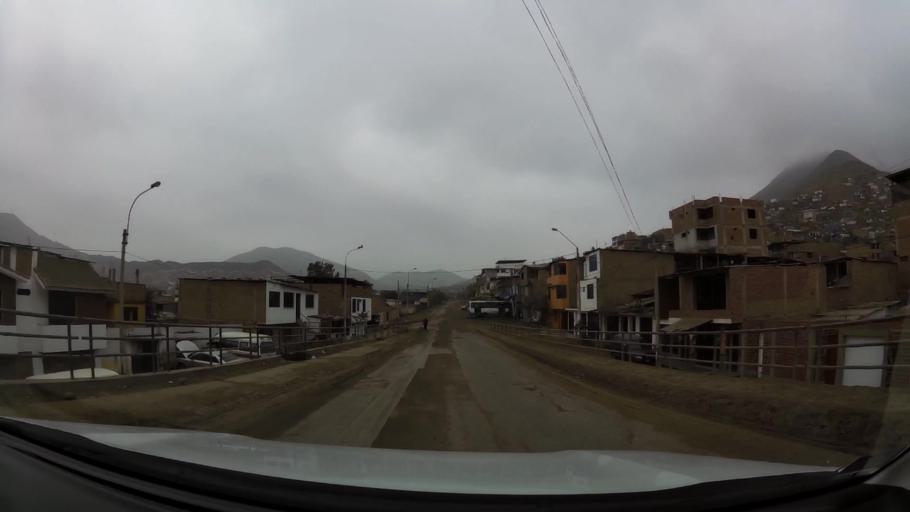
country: PE
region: Lima
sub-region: Lima
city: Cieneguilla
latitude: -12.2133
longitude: -76.9027
